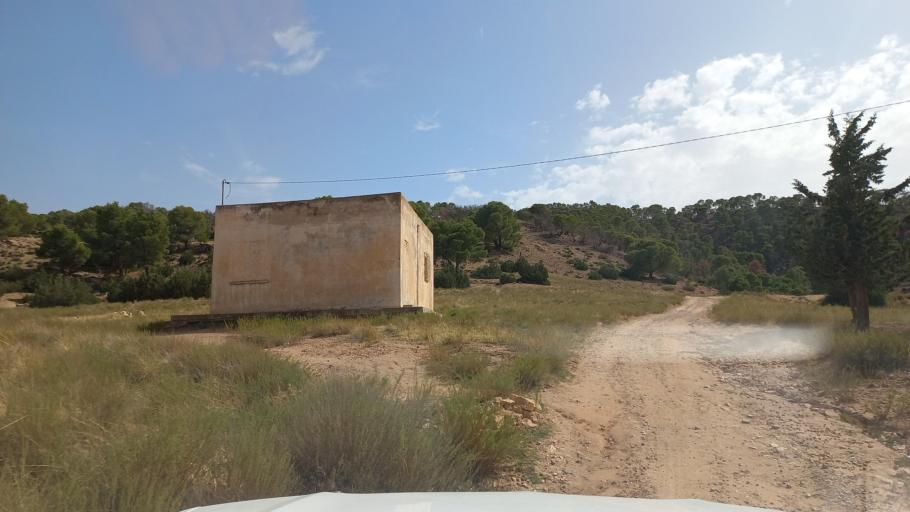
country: TN
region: Al Qasrayn
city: Kasserine
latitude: 35.3532
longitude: 8.8857
